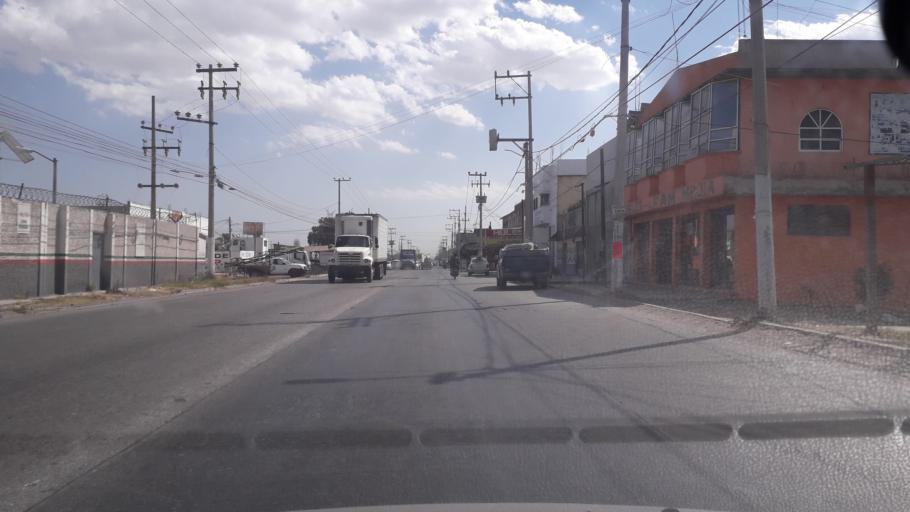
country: MX
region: Mexico
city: Ecatepec
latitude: 19.6345
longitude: -99.0546
